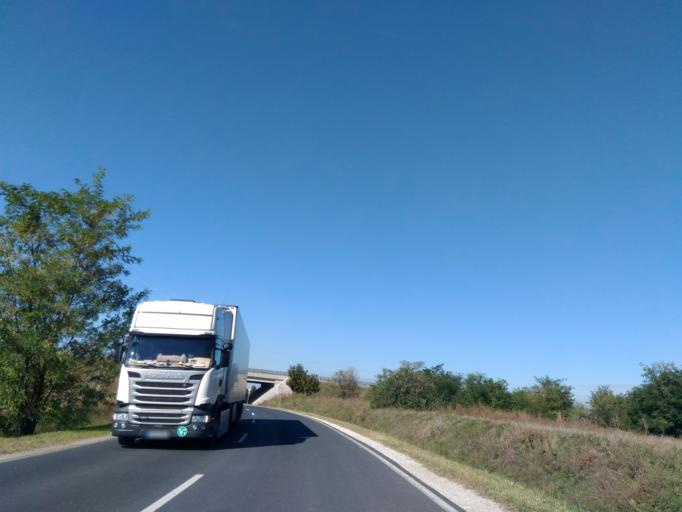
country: HU
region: Fejer
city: Ivancsa
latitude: 47.1774
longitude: 18.8086
